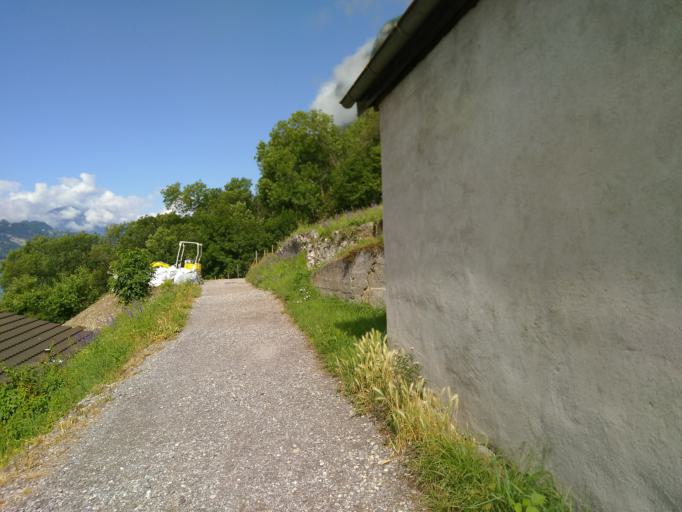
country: CH
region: Saint Gallen
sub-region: Wahlkreis Sarganserland
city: Quarten
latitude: 47.1304
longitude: 9.2071
